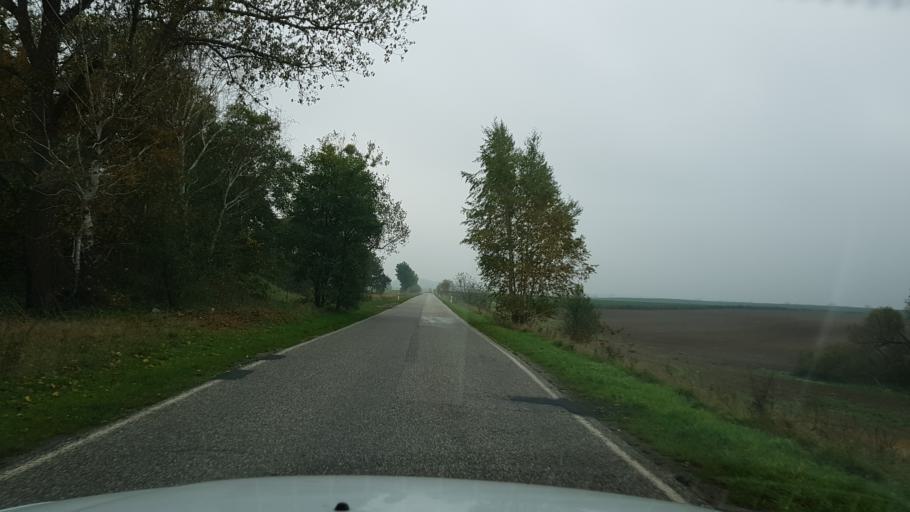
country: PL
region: West Pomeranian Voivodeship
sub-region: Powiat stargardzki
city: Dolice
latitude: 53.1759
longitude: 15.2148
